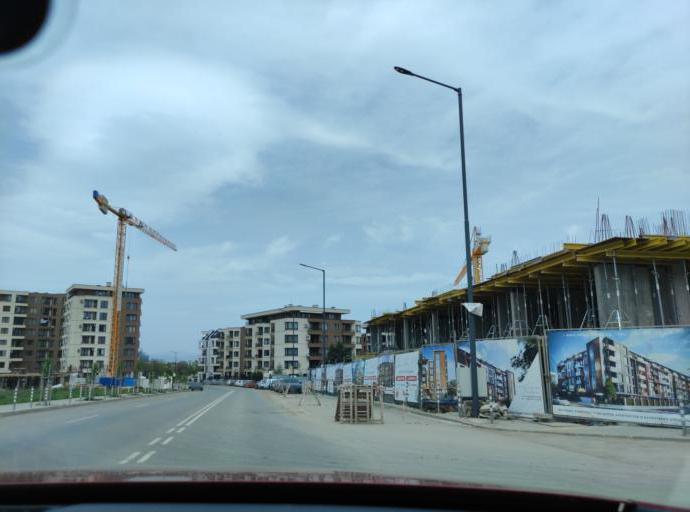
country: BG
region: Sofia-Capital
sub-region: Stolichna Obshtina
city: Sofia
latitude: 42.6410
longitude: 23.3442
